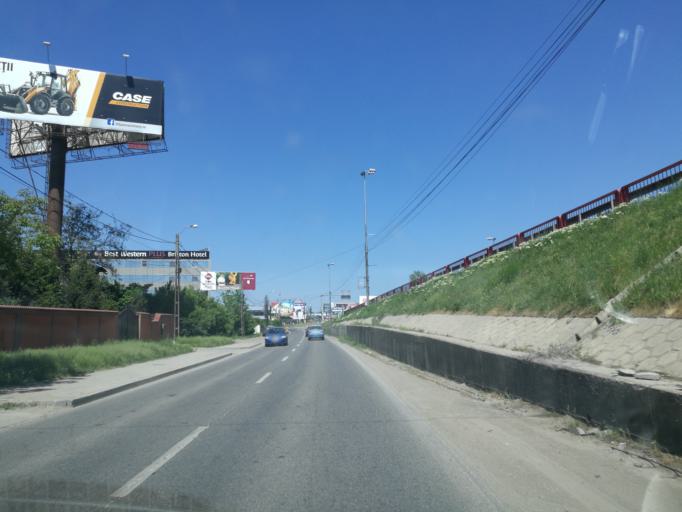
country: RO
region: Ilfov
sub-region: Comuna Otopeni
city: Otopeni
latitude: 44.5365
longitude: 26.0683
